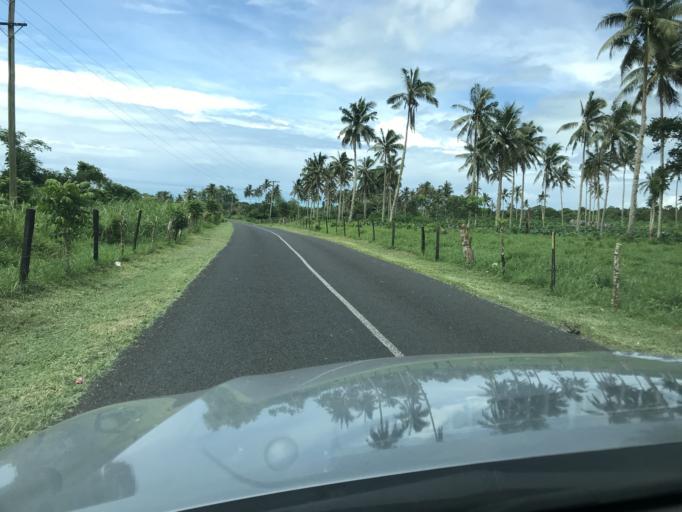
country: WS
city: Fasito`outa
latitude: -13.8695
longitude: -171.9128
